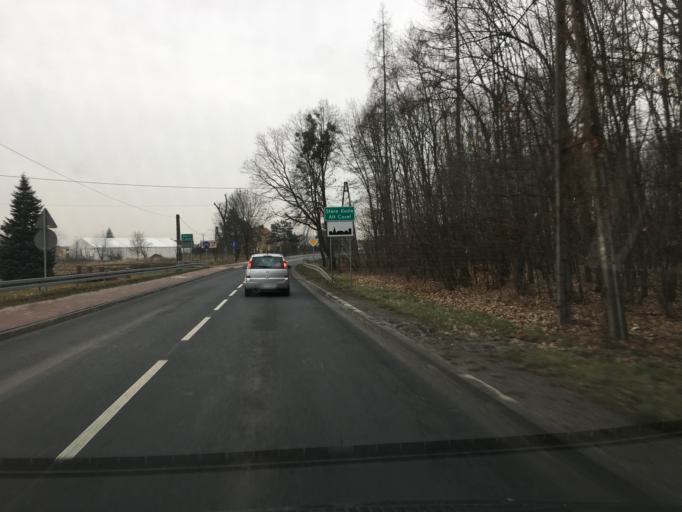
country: PL
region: Opole Voivodeship
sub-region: Powiat kedzierzynsko-kozielski
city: Kedzierzyn-Kozle
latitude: 50.3187
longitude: 18.2231
